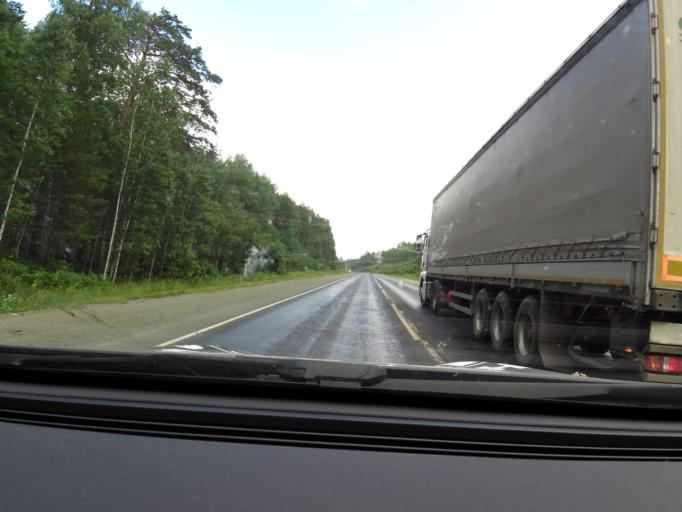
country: RU
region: Sverdlovsk
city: Bisert'
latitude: 56.8364
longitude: 58.8806
